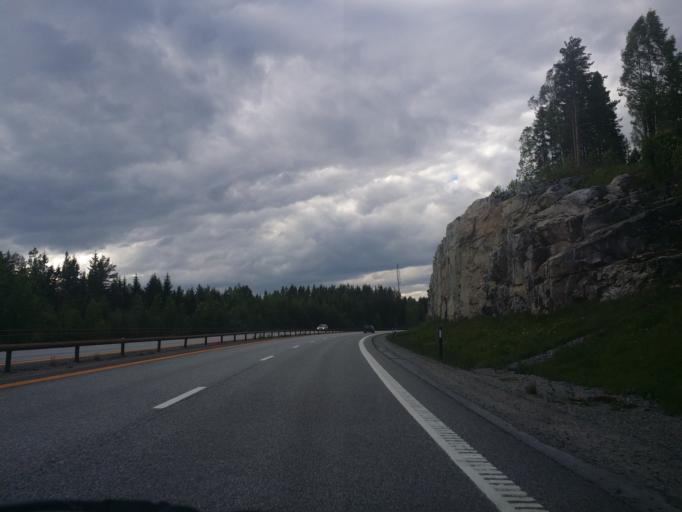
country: NO
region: Akershus
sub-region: Eidsvoll
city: Raholt
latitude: 60.2710
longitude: 11.1556
